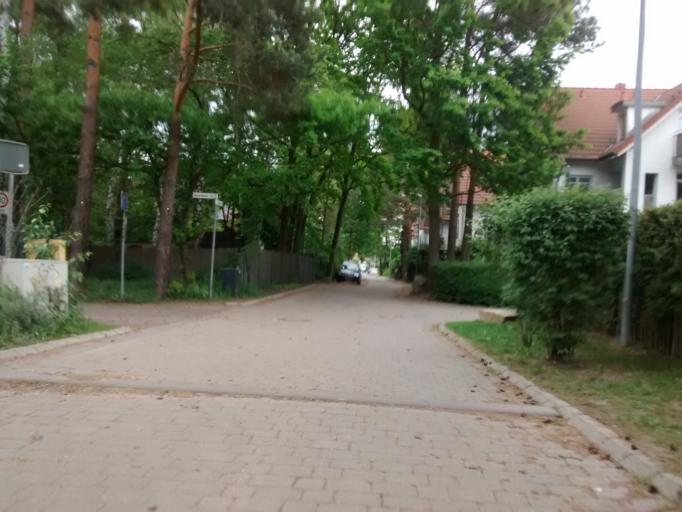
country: DE
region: Brandenburg
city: Hohen Neuendorf
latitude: 52.6714
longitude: 13.2588
